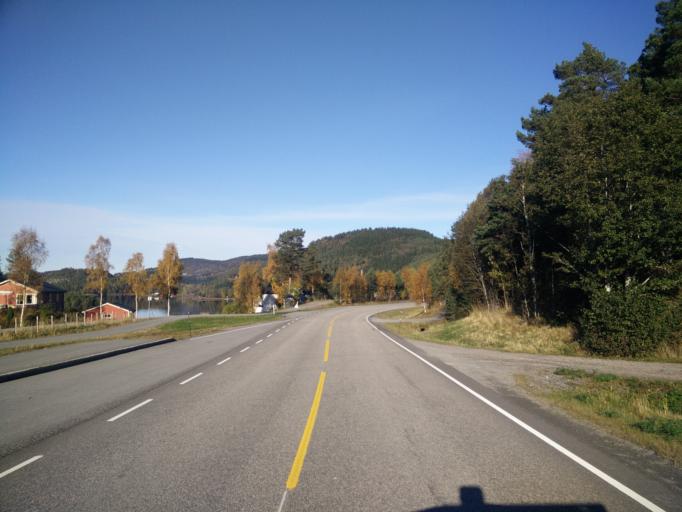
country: NO
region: More og Romsdal
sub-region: Kristiansund
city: Rensvik
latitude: 63.0146
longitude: 8.0028
